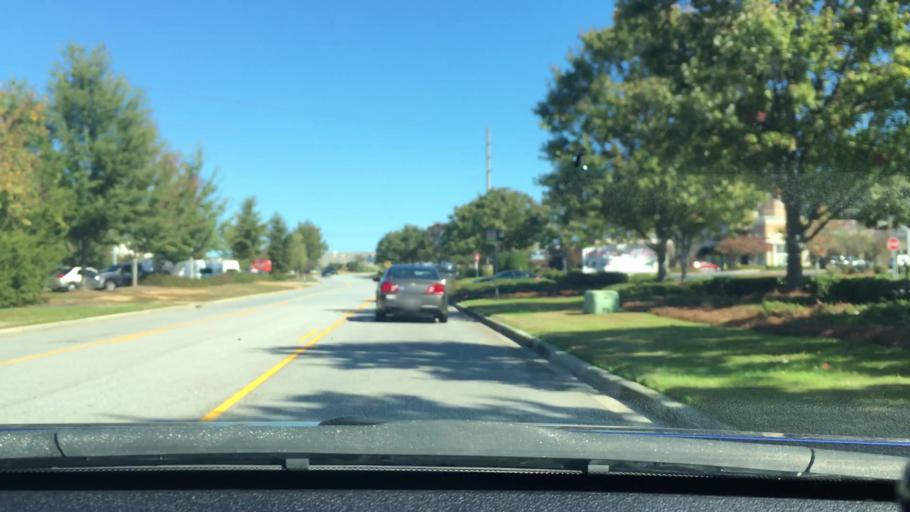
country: US
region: South Carolina
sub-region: Lexington County
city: Seven Oaks
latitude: 34.0698
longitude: -81.1547
